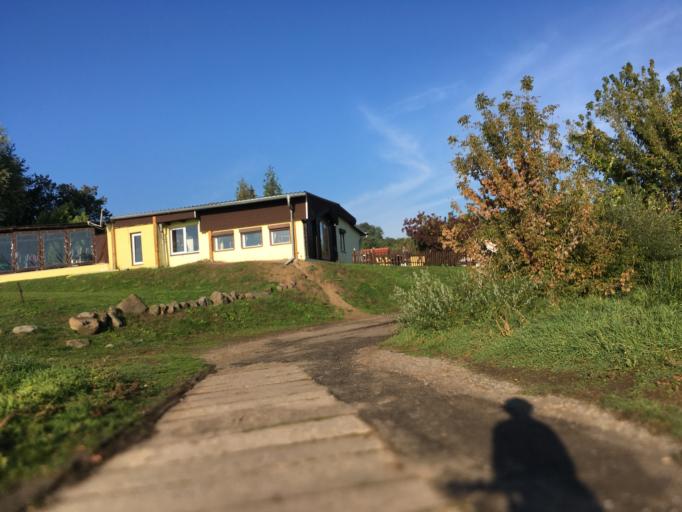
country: DE
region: Brandenburg
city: Lebus
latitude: 52.4245
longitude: 14.5427
